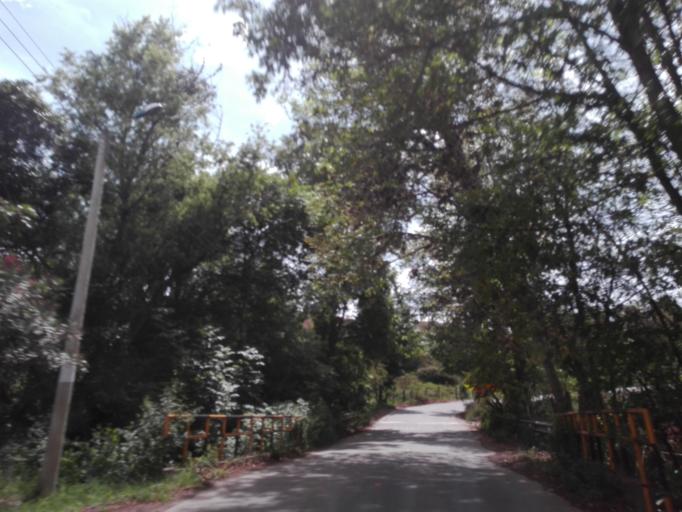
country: CO
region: Boyaca
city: Raquira
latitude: 5.5659
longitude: -73.6498
